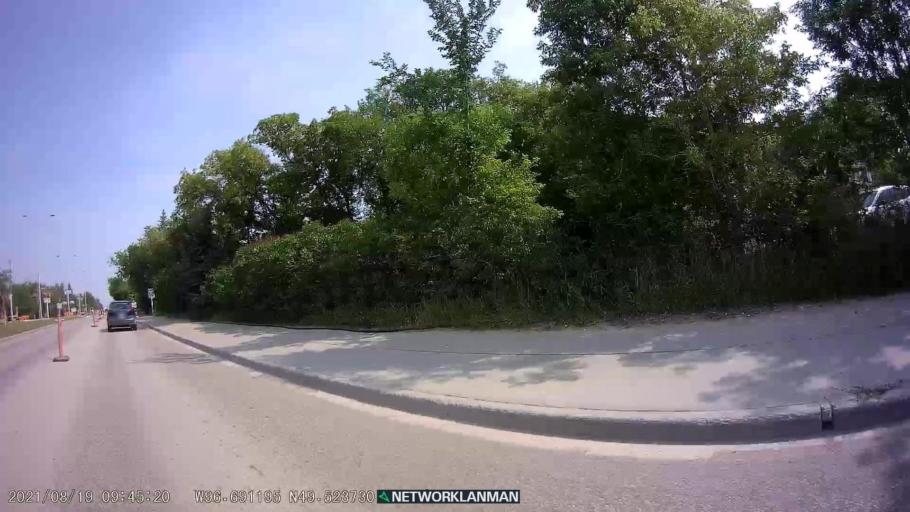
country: CA
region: Manitoba
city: Steinbach
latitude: 49.5238
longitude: -96.6911
